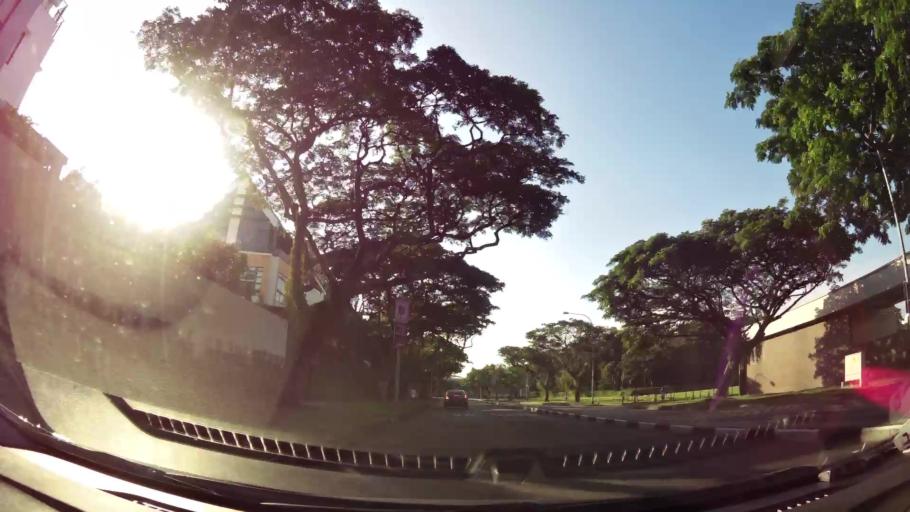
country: SG
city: Singapore
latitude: 1.3194
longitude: 103.9475
